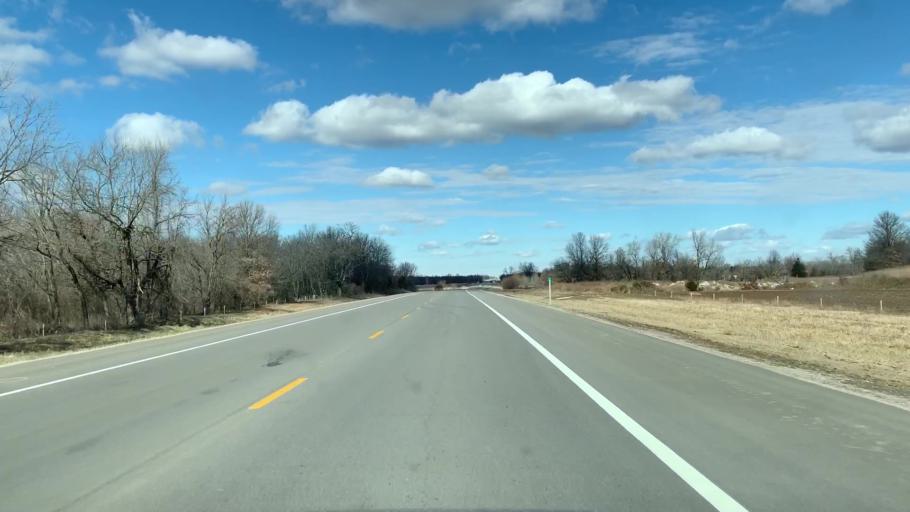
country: US
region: Kansas
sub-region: Cherokee County
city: Columbus
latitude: 37.2596
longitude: -94.8319
